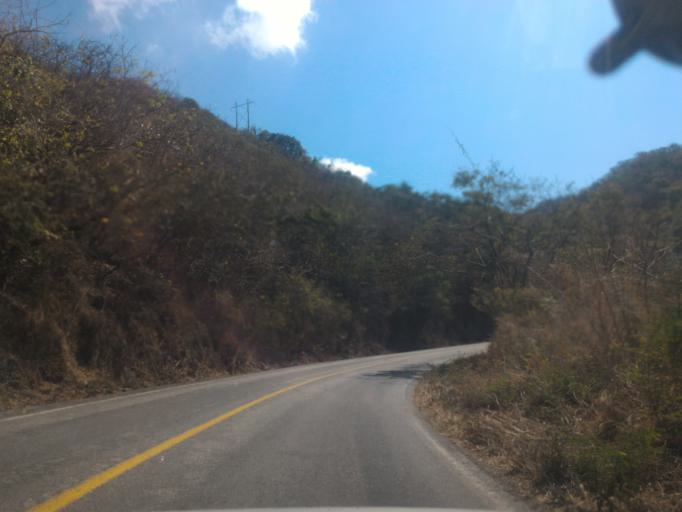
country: MX
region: Michoacan
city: Coahuayana Viejo
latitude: 18.5709
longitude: -103.6576
